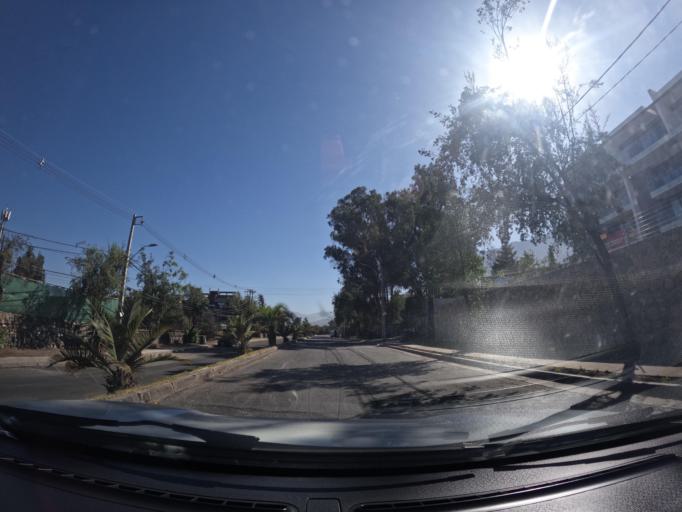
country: CL
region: Santiago Metropolitan
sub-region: Provincia de Santiago
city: Villa Presidente Frei, Nunoa, Santiago, Chile
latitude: -33.4968
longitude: -70.5309
